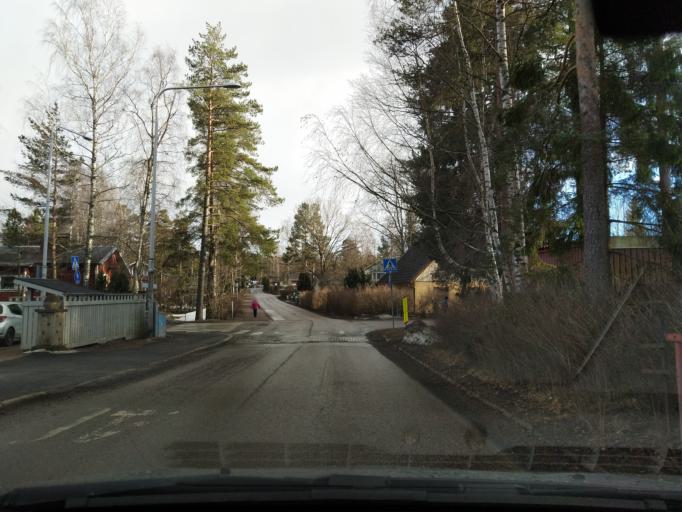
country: FI
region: Uusimaa
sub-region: Helsinki
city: Vantaa
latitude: 60.2828
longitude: 25.0674
